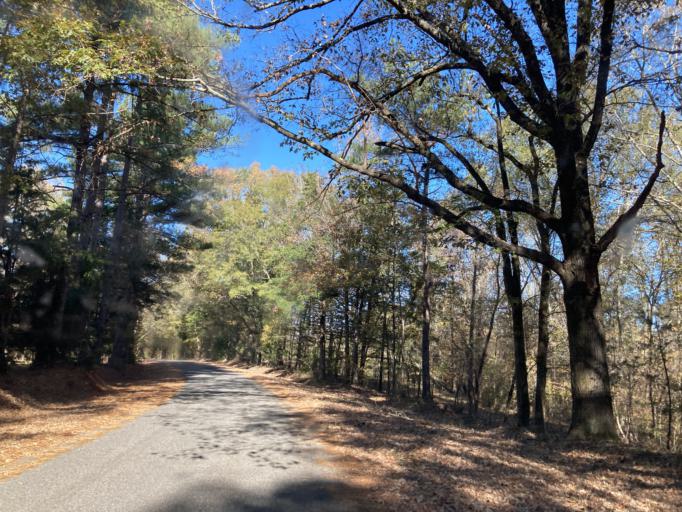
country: US
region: Mississippi
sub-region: Hinds County
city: Lynchburg
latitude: 32.5749
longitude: -90.5488
